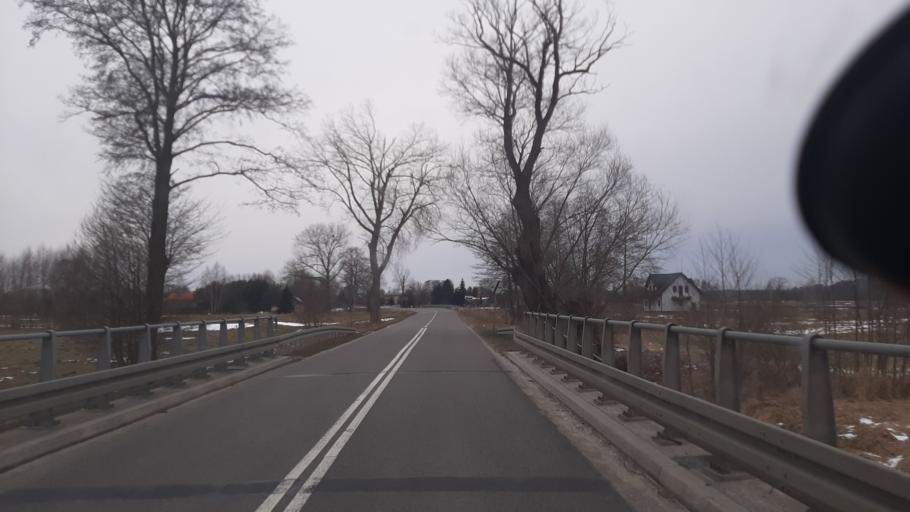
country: PL
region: Lublin Voivodeship
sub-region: Powiat lubartowski
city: Kamionka
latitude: 51.4875
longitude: 22.4444
